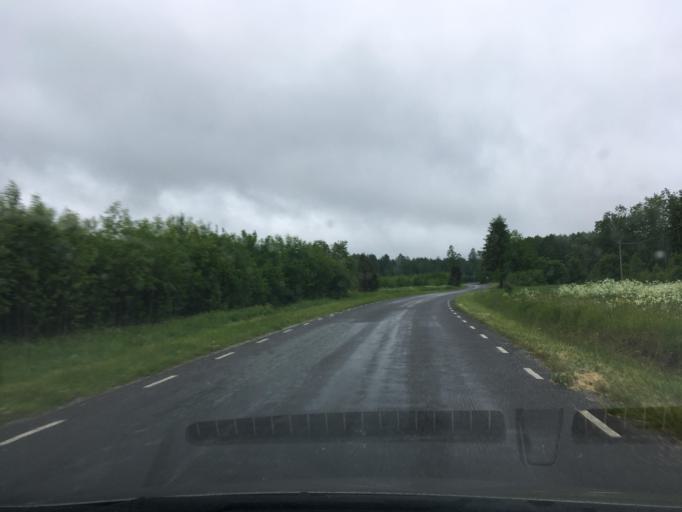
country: EE
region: Laeaene
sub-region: Lihula vald
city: Lihula
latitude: 58.6549
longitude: 23.7745
